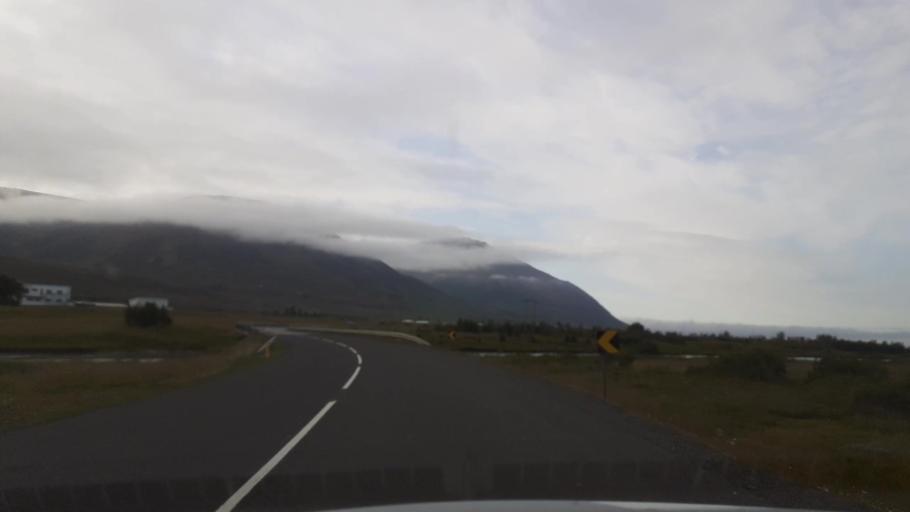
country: IS
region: Northeast
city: Dalvik
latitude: 65.9588
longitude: -18.5373
